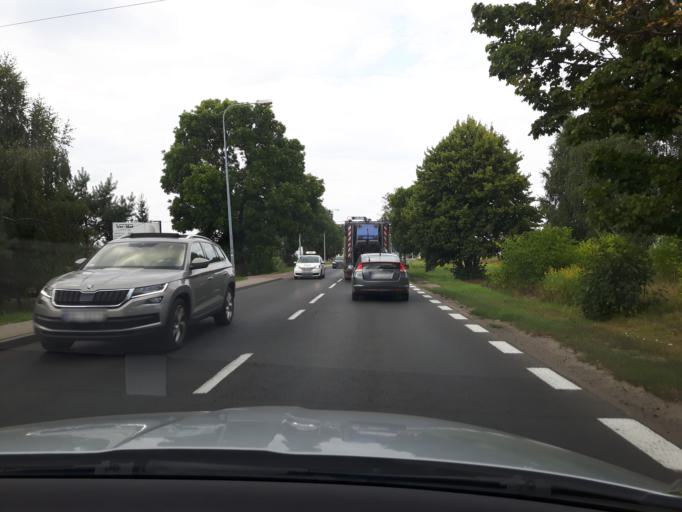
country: PL
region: Masovian Voivodeship
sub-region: Powiat legionowski
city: Stanislawow Pierwszy
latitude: 52.3608
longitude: 21.0283
